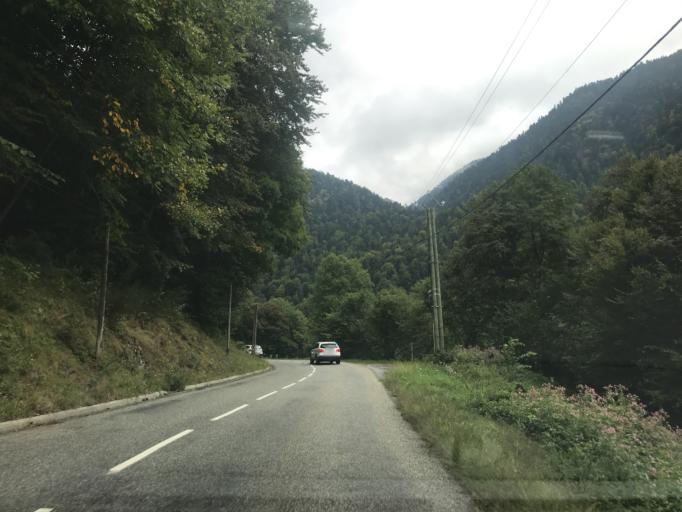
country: FR
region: Midi-Pyrenees
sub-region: Departement de la Haute-Garonne
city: Bagneres-de-Luchon
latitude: 42.7694
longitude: 0.6379
